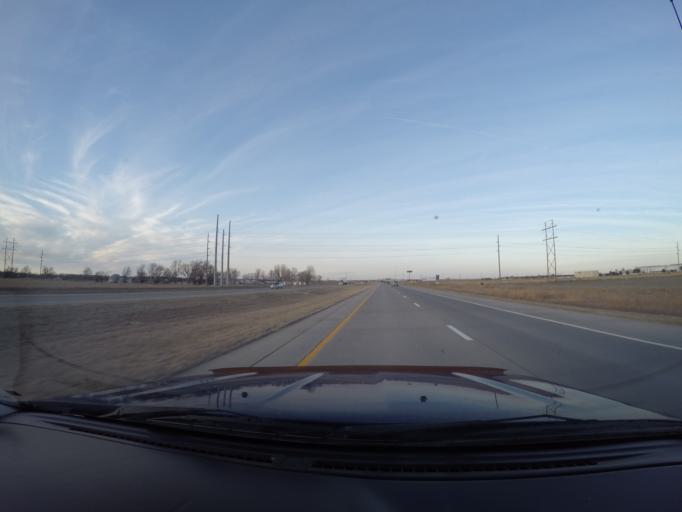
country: US
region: Kansas
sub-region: Saline County
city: Salina
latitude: 38.7606
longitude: -97.6180
